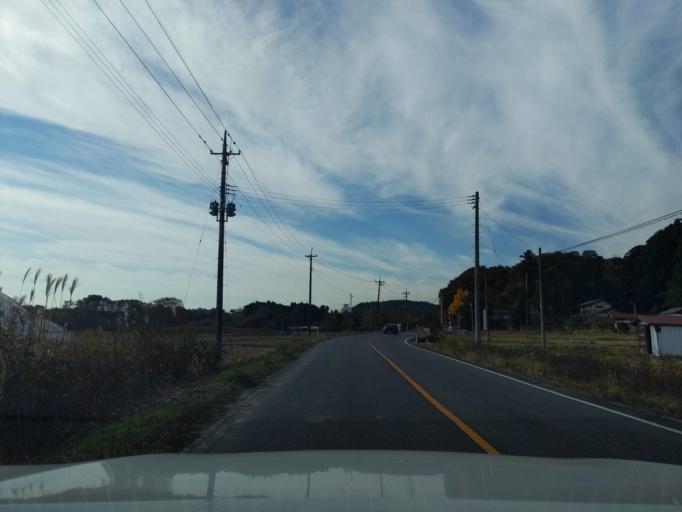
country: JP
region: Fukushima
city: Koriyama
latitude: 37.4166
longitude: 140.2995
